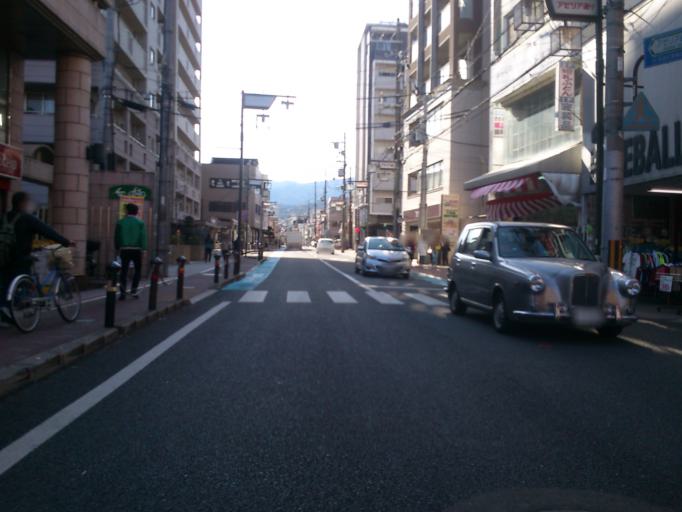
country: JP
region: Kyoto
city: Muko
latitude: 34.9263
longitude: 135.6925
